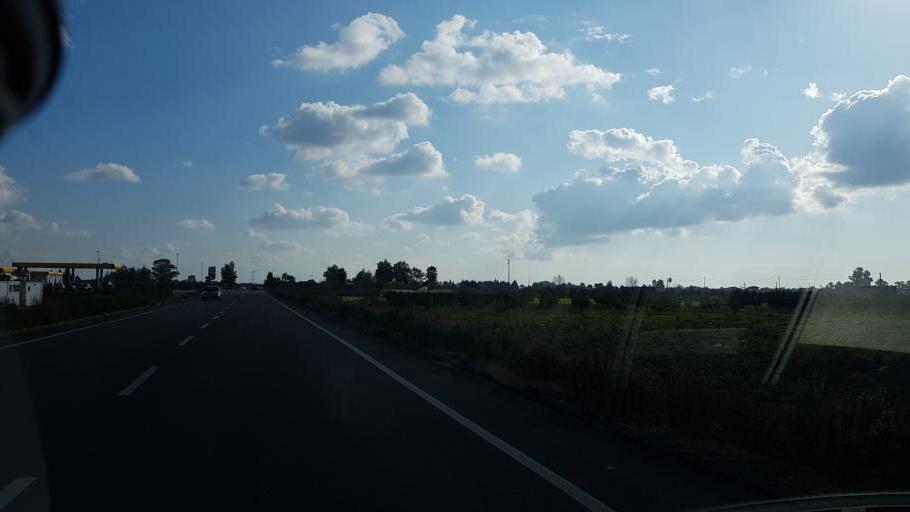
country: IT
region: Apulia
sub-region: Provincia di Lecce
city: Veglie
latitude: 40.3427
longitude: 17.9775
